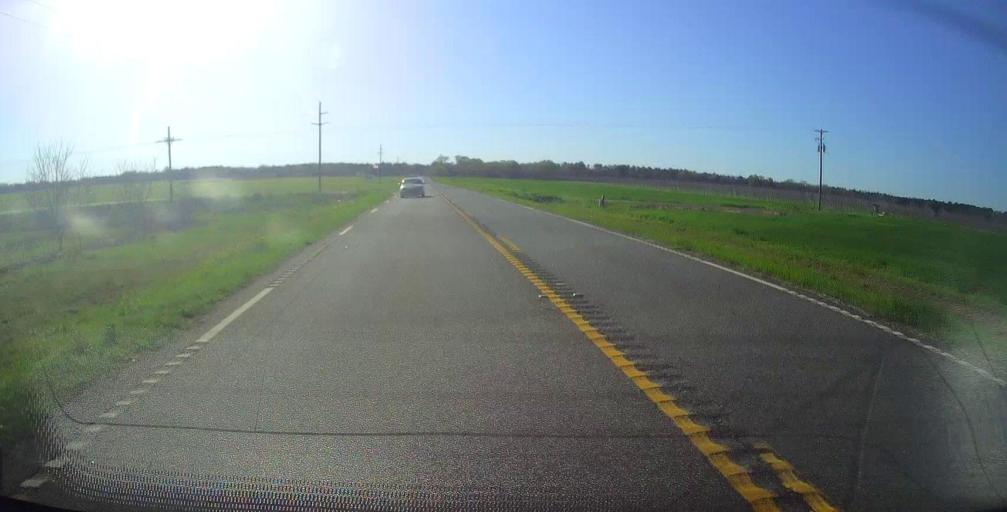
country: US
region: Georgia
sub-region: Macon County
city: Marshallville
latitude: 32.4395
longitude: -83.8746
